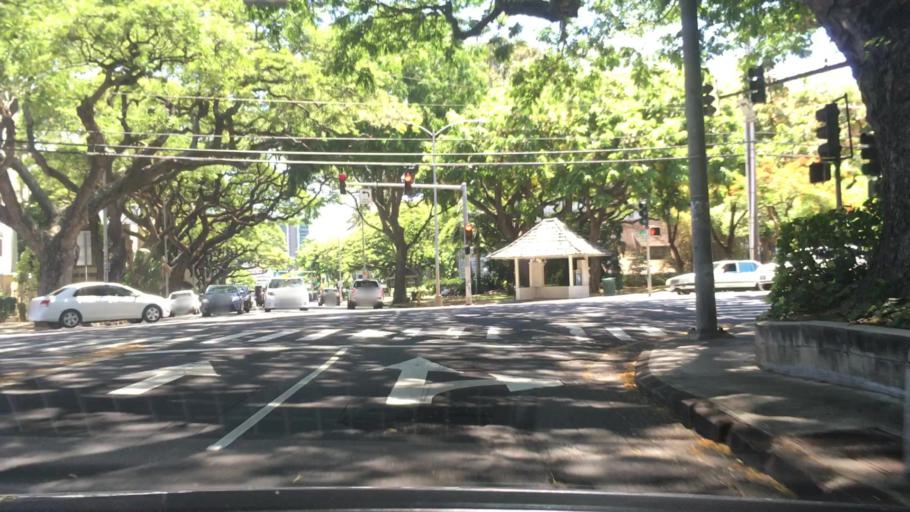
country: US
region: Hawaii
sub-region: Honolulu County
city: Honolulu
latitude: 21.3031
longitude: -157.8324
